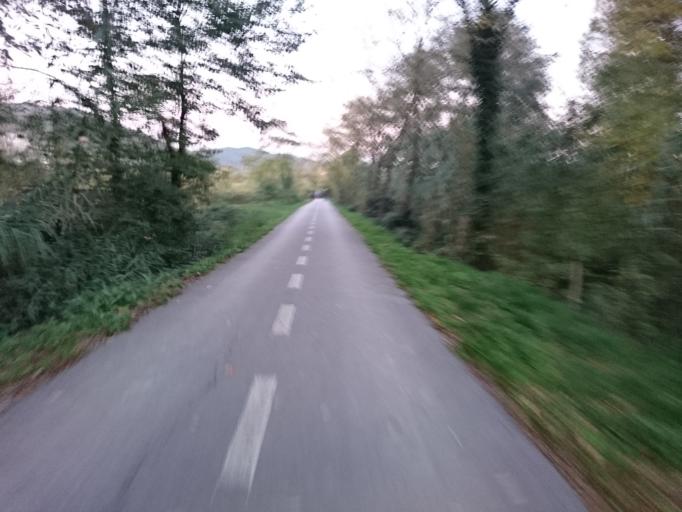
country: SI
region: Koper-Capodistria
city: Pobegi
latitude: 45.5507
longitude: 13.7912
